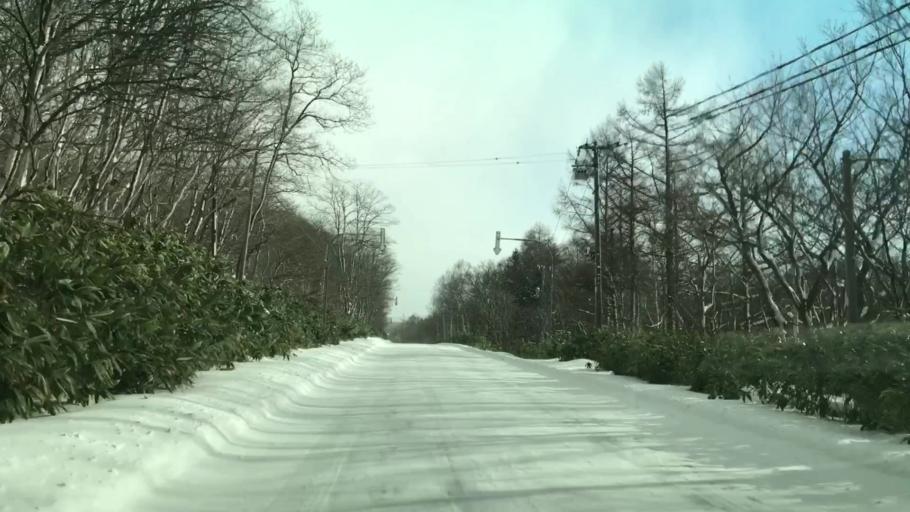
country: JP
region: Hokkaido
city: Yoichi
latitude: 43.3207
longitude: 140.5195
